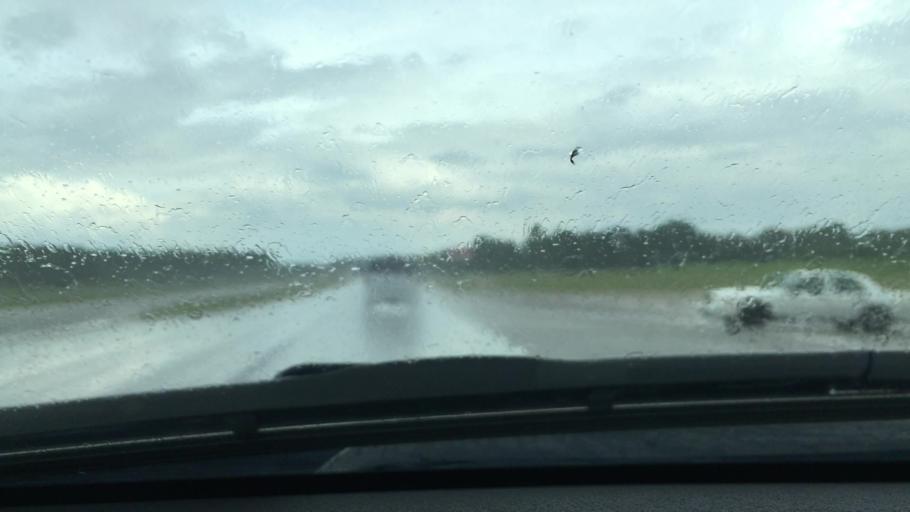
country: US
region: South Carolina
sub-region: Sumter County
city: Cherryvale
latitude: 33.9598
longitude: -80.4751
